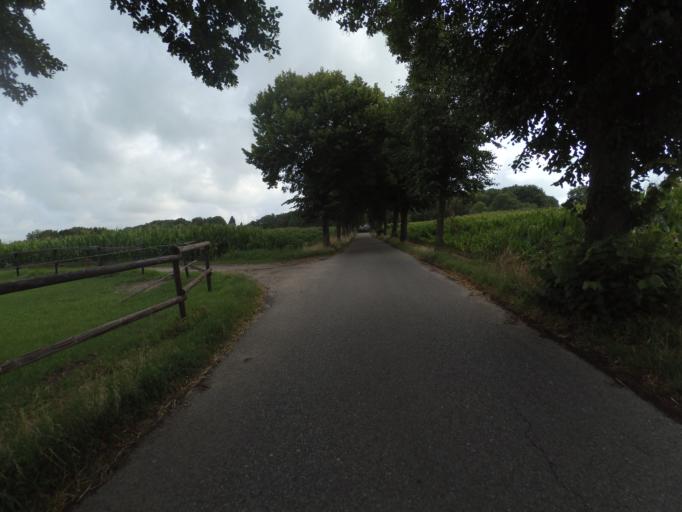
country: DE
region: North Rhine-Westphalia
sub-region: Regierungsbezirk Koln
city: Selfkant
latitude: 51.0508
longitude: 5.9065
